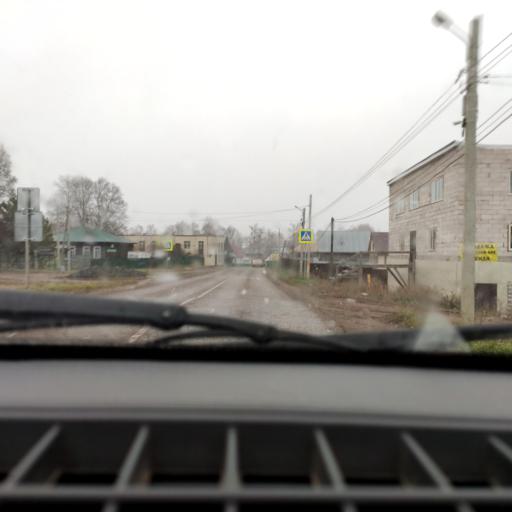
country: RU
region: Bashkortostan
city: Avdon
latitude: 54.6551
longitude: 55.7605
